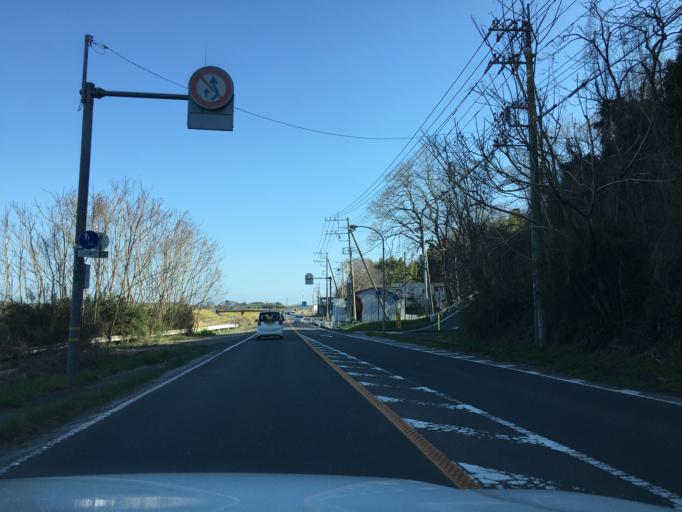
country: JP
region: Ibaraki
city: Mito-shi
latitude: 36.4400
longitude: 140.4143
